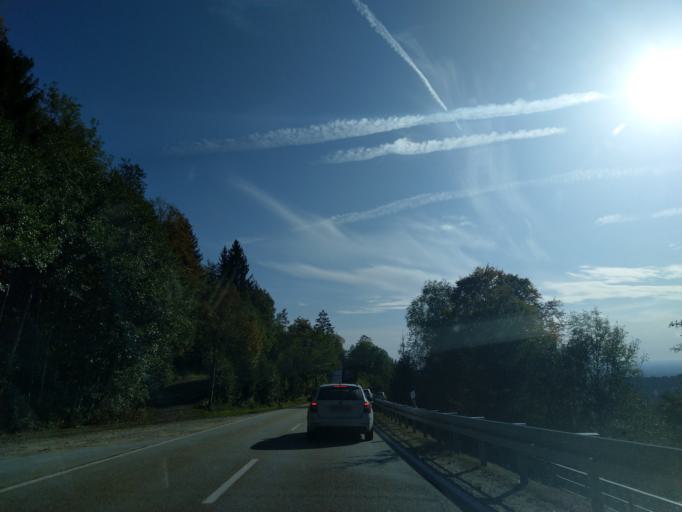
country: DE
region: Bavaria
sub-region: Lower Bavaria
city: Achslach
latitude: 48.9310
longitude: 12.9266
